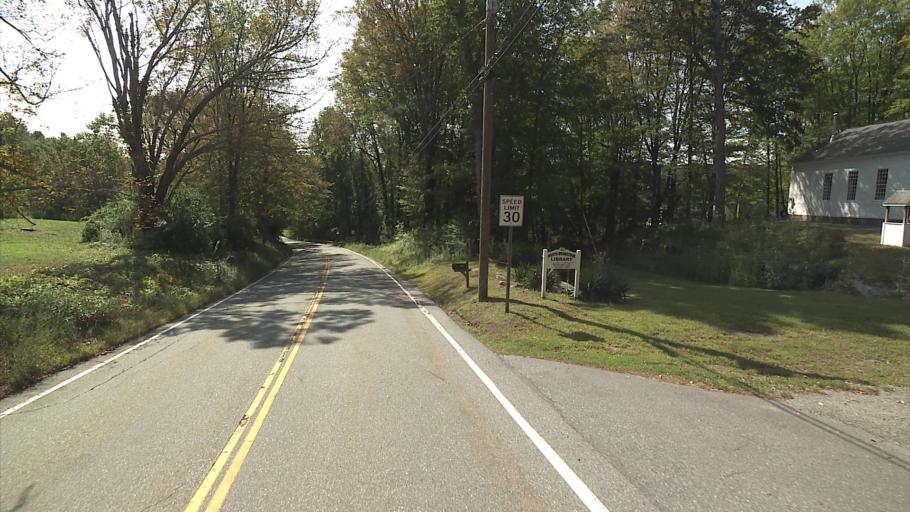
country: US
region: Connecticut
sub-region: Windham County
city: Quinebaug
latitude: 41.9957
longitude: -71.9995
